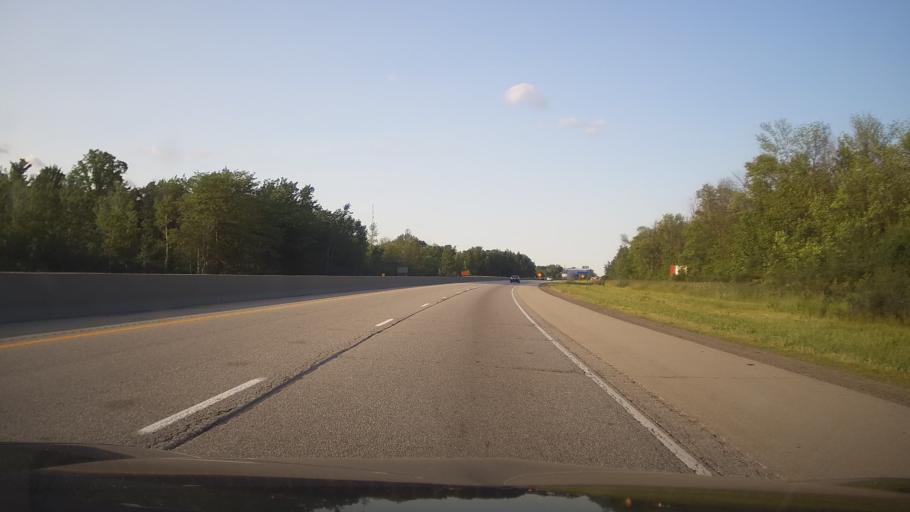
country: CA
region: Ontario
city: Brockville
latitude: 44.6392
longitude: -75.6446
